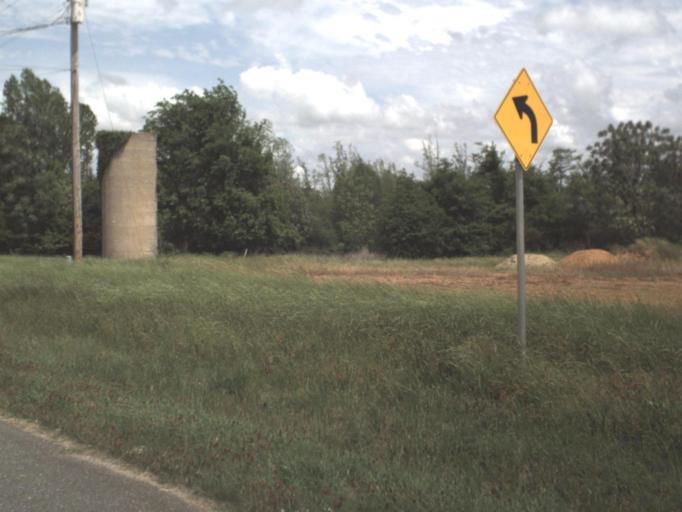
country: US
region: Alabama
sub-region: Escambia County
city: East Brewton
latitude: 30.9797
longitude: -87.1205
